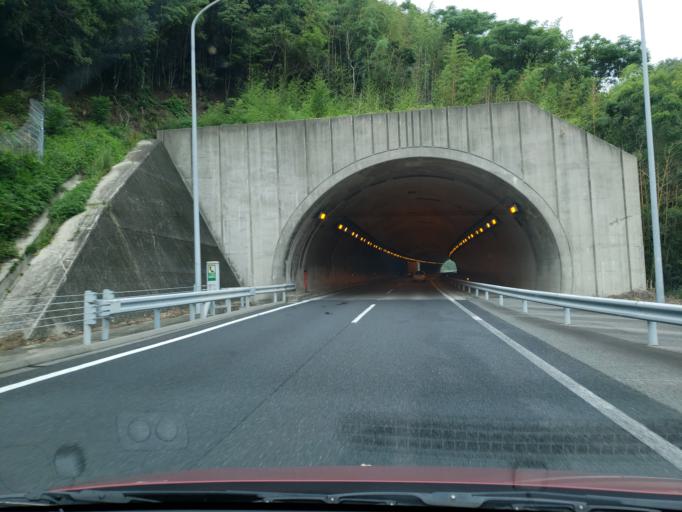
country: JP
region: Hyogo
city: Akashi
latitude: 34.5297
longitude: 134.9260
